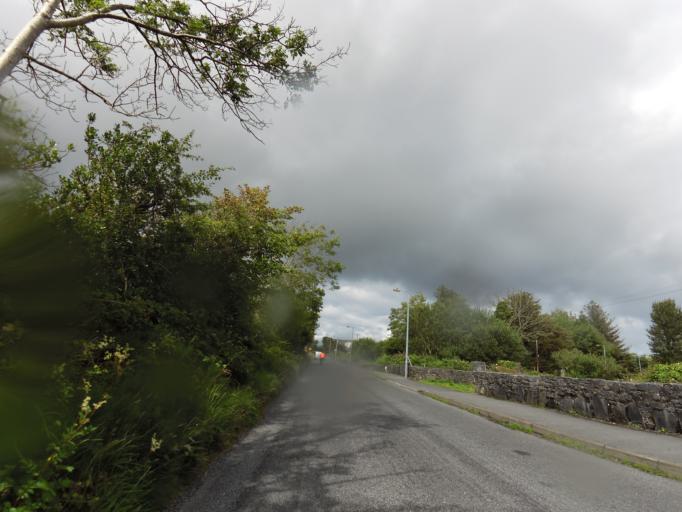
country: IE
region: Connaught
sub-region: County Galway
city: Oughterard
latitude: 53.4260
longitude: -9.3270
